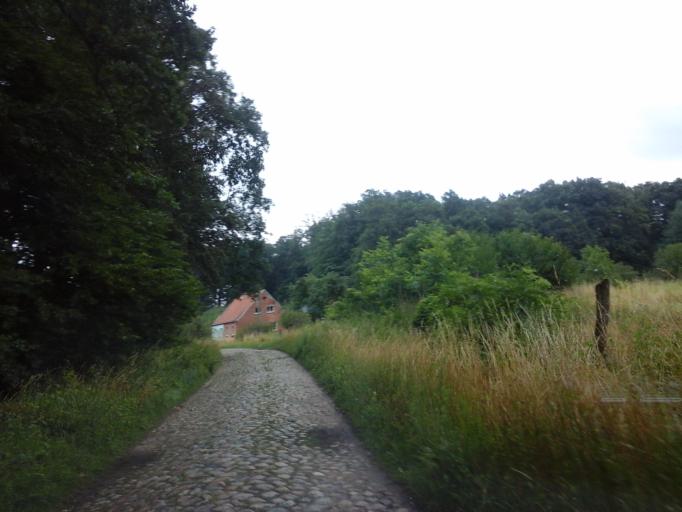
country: PL
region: West Pomeranian Voivodeship
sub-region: Powiat choszczenski
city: Krzecin
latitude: 53.0109
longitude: 15.4641
